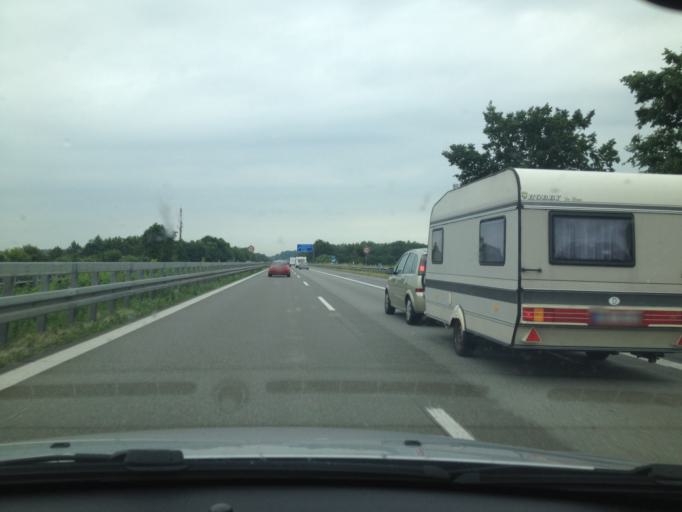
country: DE
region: Baden-Wuerttemberg
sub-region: Tuebingen Region
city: Setzingen
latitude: 48.5702
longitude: 10.1524
